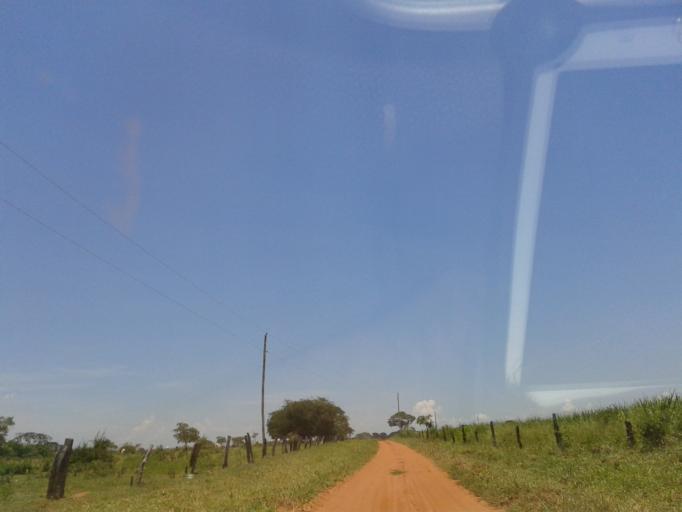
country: BR
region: Minas Gerais
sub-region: Santa Vitoria
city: Santa Vitoria
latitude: -19.2260
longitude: -50.4579
